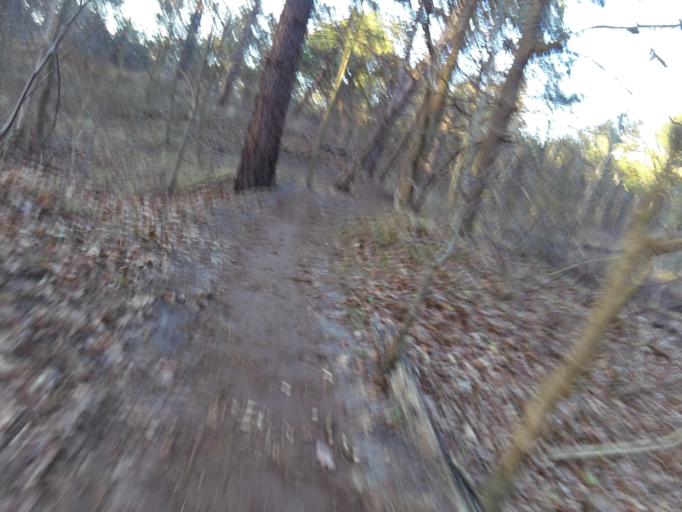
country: NL
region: South Holland
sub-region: Gemeente Noordwijkerhout
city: Noordwijkerhout
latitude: 52.2685
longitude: 4.4606
